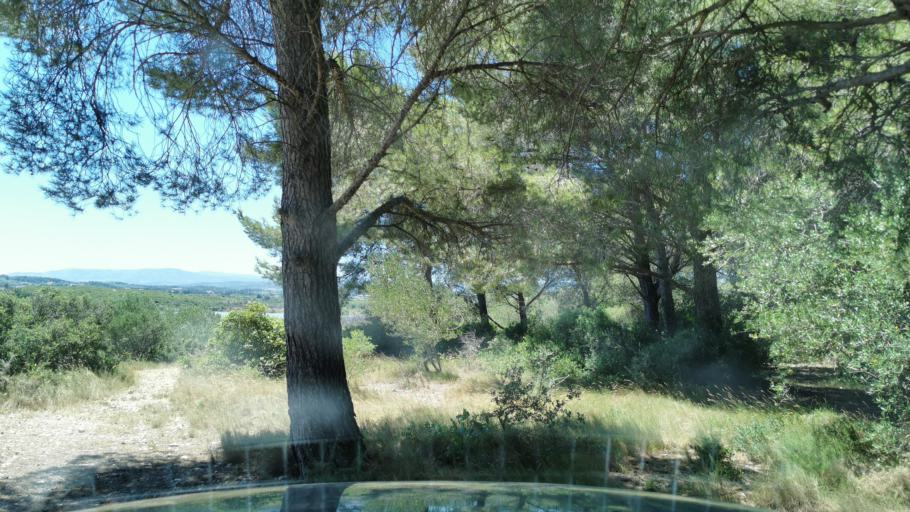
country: FR
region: Languedoc-Roussillon
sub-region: Departement de l'Aude
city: Peyriac-de-Mer
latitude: 43.1104
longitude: 2.9646
